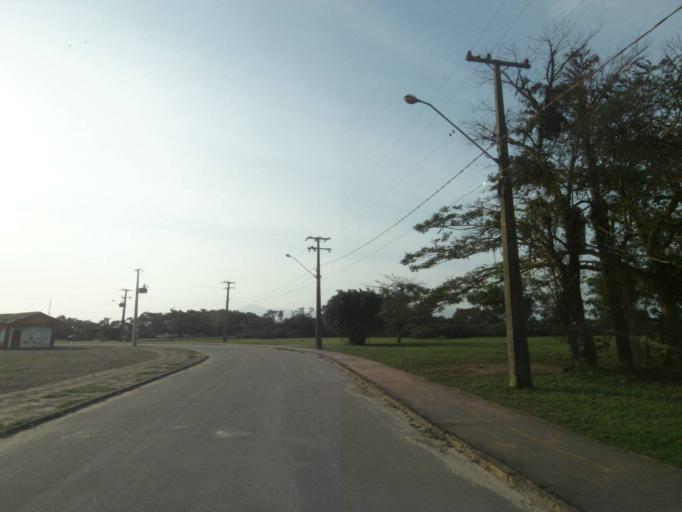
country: BR
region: Parana
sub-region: Paranagua
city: Paranagua
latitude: -25.5054
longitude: -48.5307
